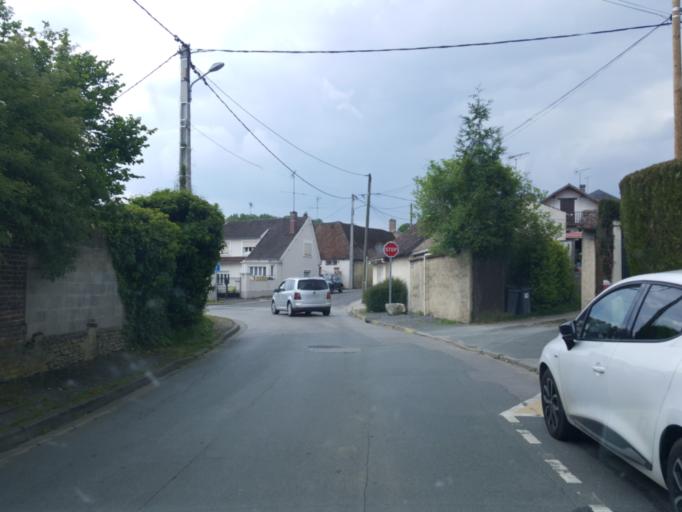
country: FR
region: Picardie
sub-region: Departement de l'Oise
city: Allonne
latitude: 49.4243
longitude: 2.1325
